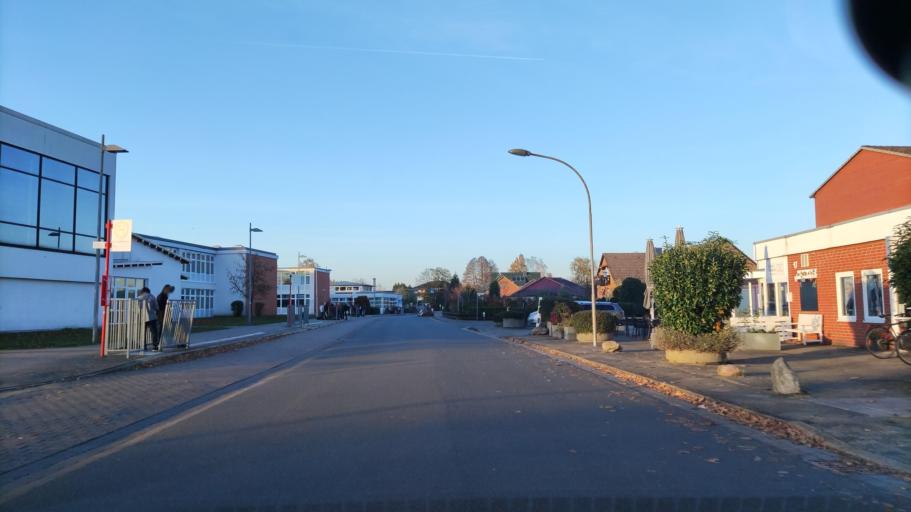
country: DE
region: Lower Saxony
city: Bleckede
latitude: 53.2851
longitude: 10.7313
